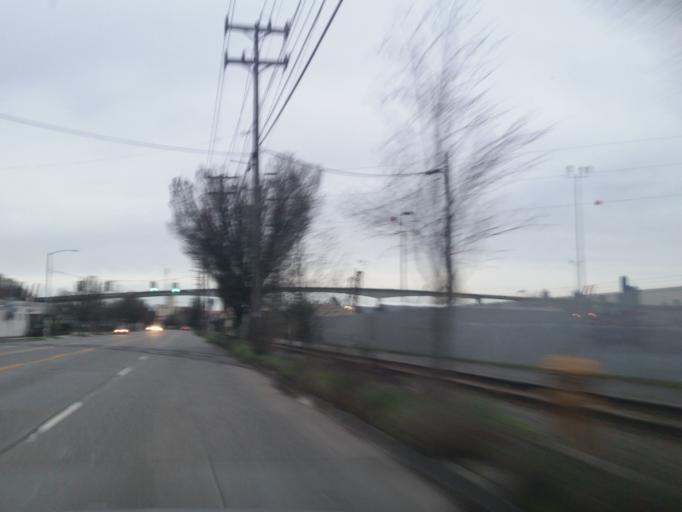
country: US
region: Washington
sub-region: King County
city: White Center
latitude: 47.5634
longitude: -122.3523
